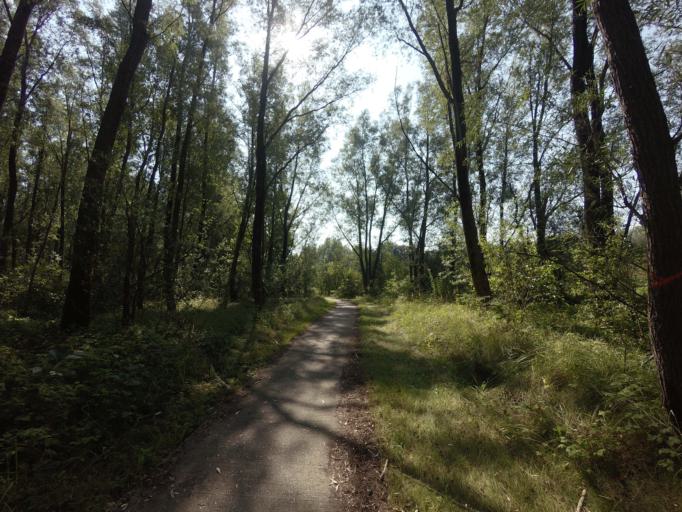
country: NL
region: Groningen
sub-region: Gemeente De Marne
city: Ulrum
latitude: 53.3912
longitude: 6.2580
